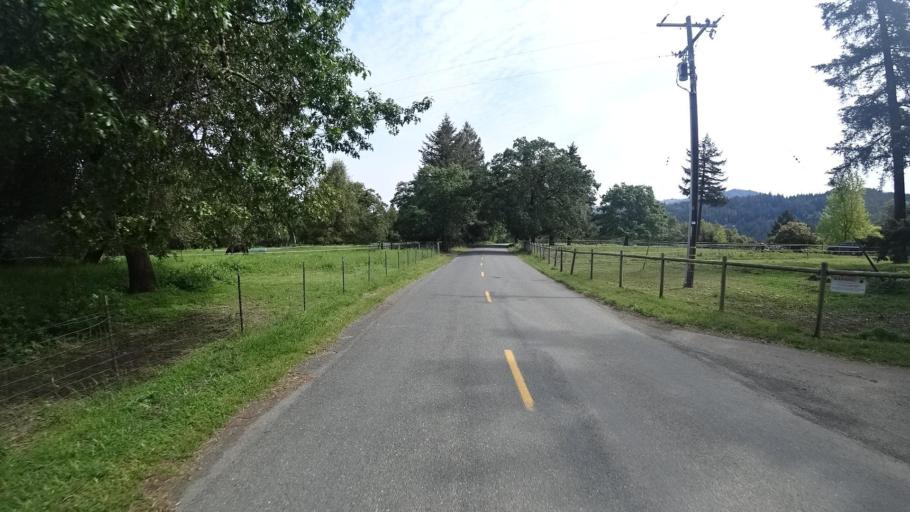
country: US
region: California
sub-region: Humboldt County
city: Redway
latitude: 40.0888
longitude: -123.8095
